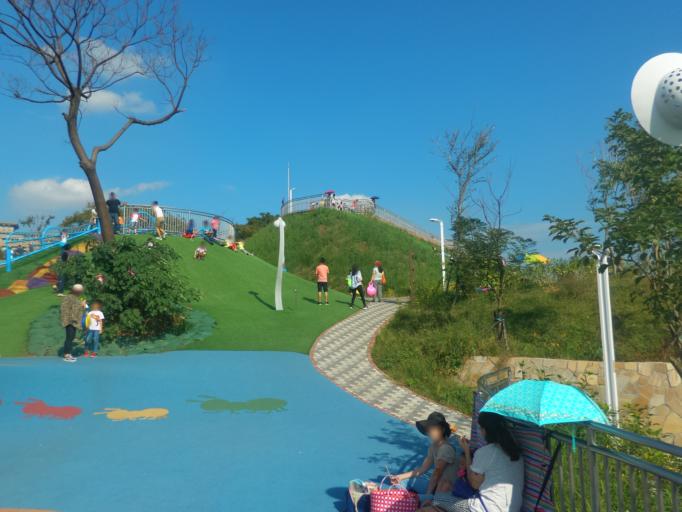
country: TW
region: Taipei
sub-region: Taipei
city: Banqiao
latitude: 25.0029
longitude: 121.4778
